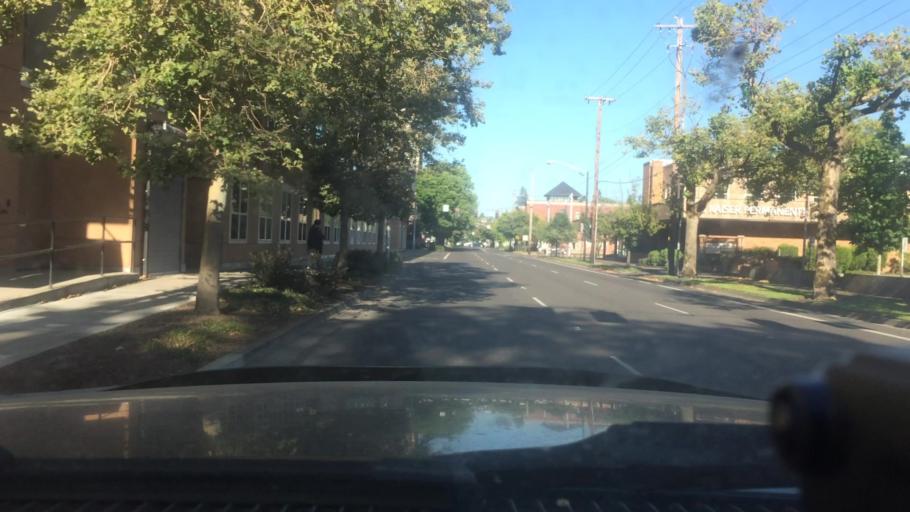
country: US
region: Oregon
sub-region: Lane County
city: Eugene
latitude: 44.0456
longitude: -123.0958
